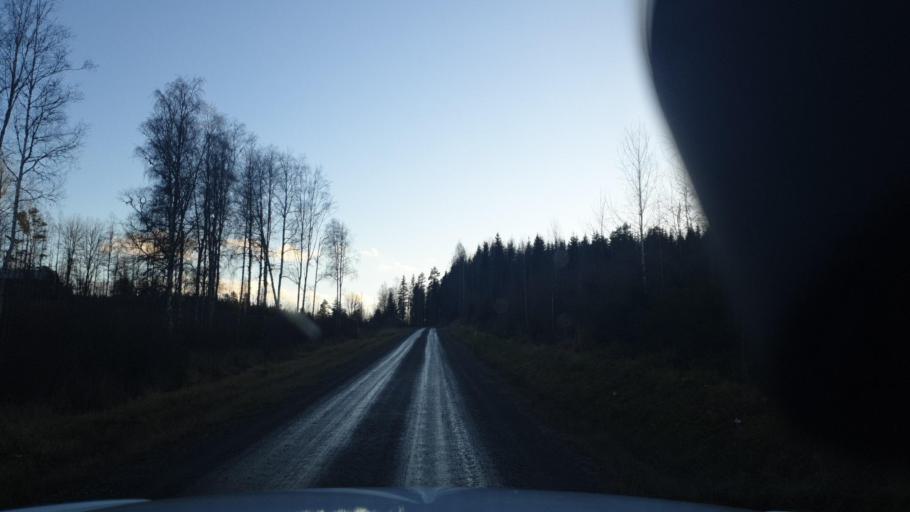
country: SE
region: Vaermland
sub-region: Eda Kommun
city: Charlottenberg
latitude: 60.0345
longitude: 12.5112
